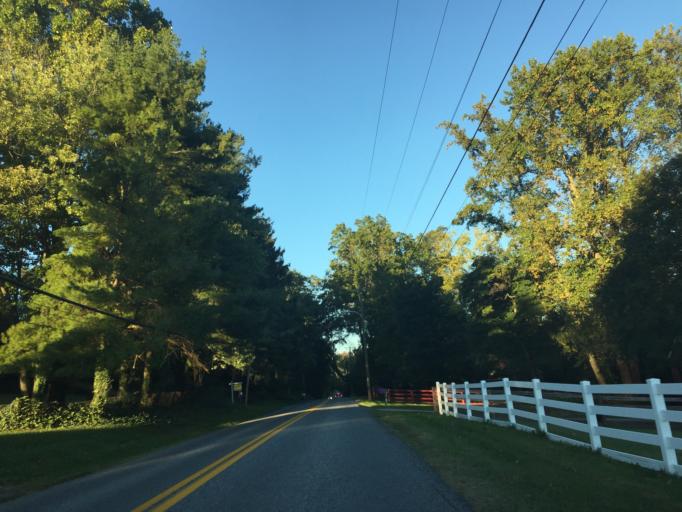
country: US
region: Maryland
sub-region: Baltimore County
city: Kingsville
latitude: 39.4503
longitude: -76.4158
